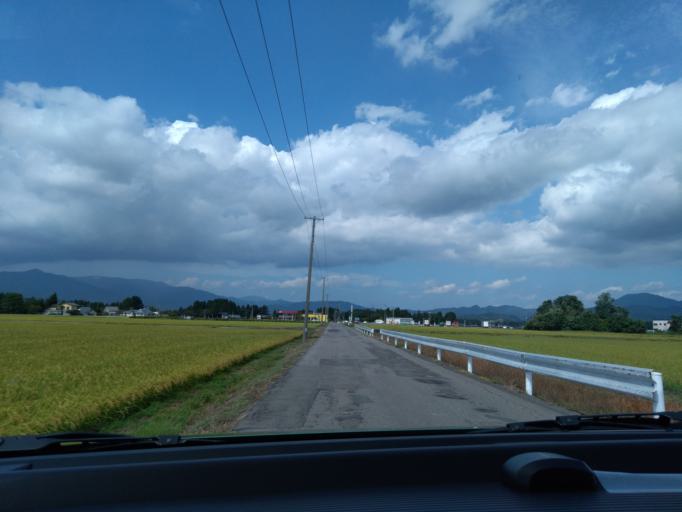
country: JP
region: Akita
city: Kakunodatemachi
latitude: 39.6102
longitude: 140.5843
